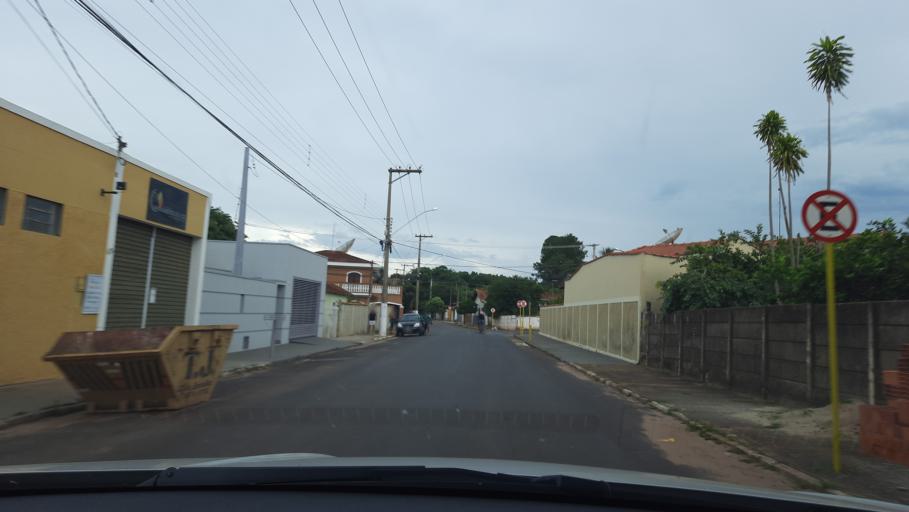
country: BR
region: Sao Paulo
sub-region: Casa Branca
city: Casa Branca
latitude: -21.7685
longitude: -47.0900
